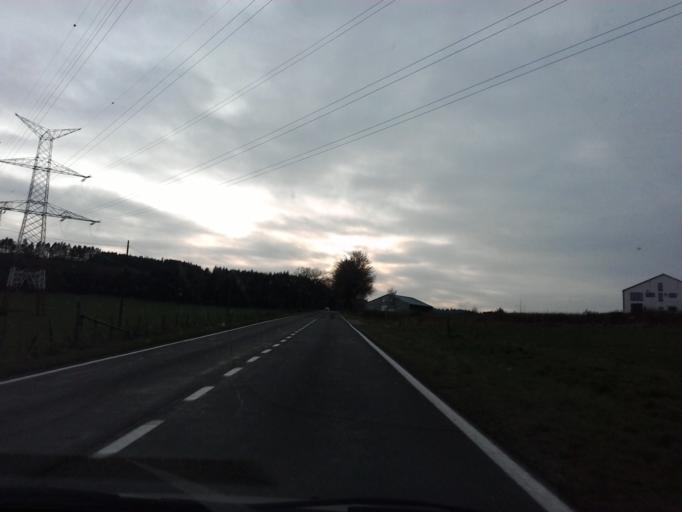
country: BE
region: Wallonia
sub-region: Province de Liege
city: Lierneux
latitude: 50.2617
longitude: 5.8264
